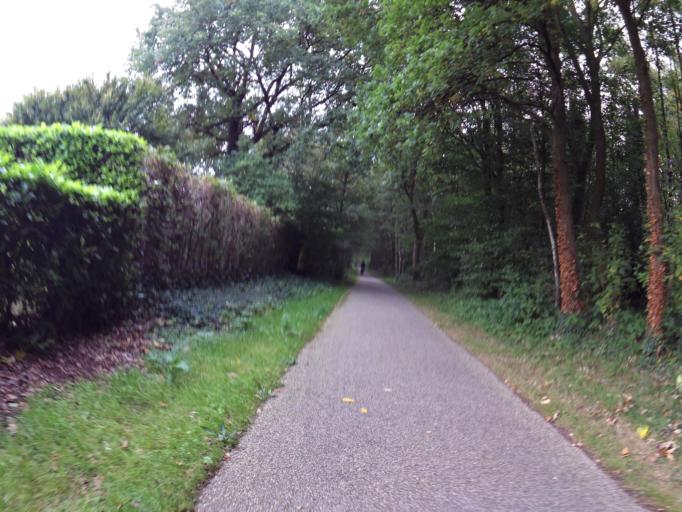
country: BE
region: Flanders
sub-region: Provincie Limburg
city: As
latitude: 51.0083
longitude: 5.6085
